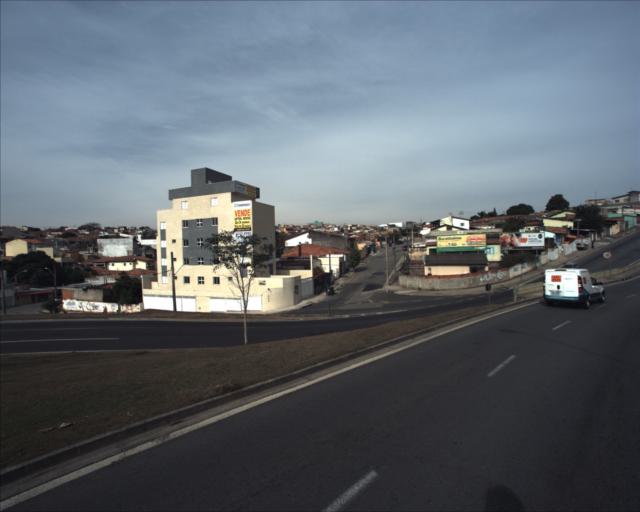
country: BR
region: Sao Paulo
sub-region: Sorocaba
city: Sorocaba
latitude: -23.4822
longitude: -47.4609
